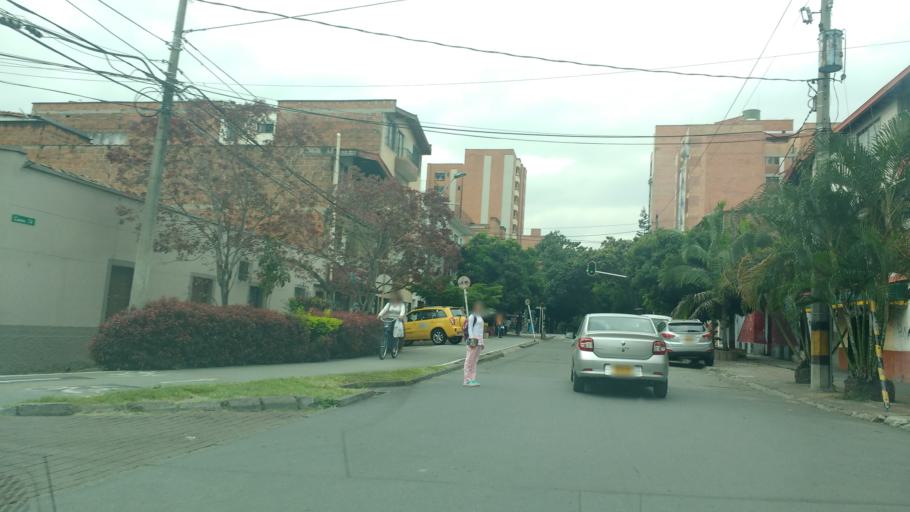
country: CO
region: Antioquia
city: Medellin
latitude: 6.2505
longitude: -75.5934
